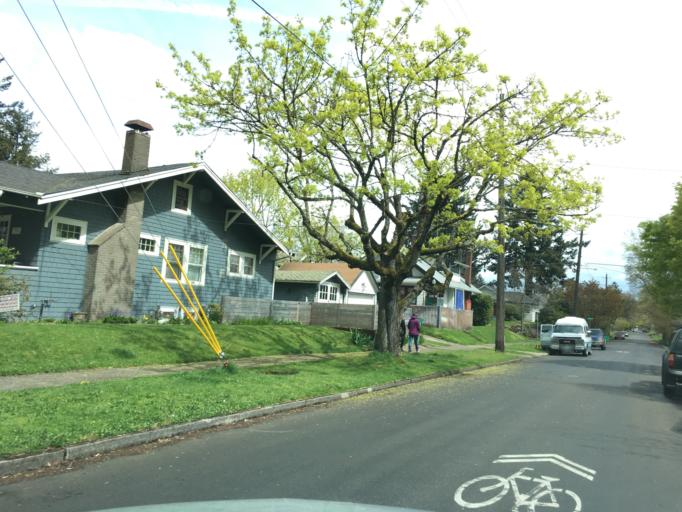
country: US
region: Oregon
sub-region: Multnomah County
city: Lents
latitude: 45.5469
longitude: -122.6014
